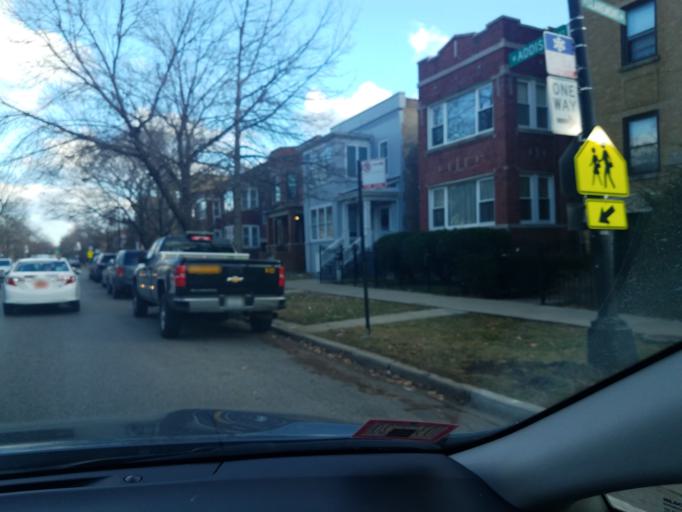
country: US
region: Illinois
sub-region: Cook County
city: Lincolnwood
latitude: 41.9467
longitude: -87.6869
